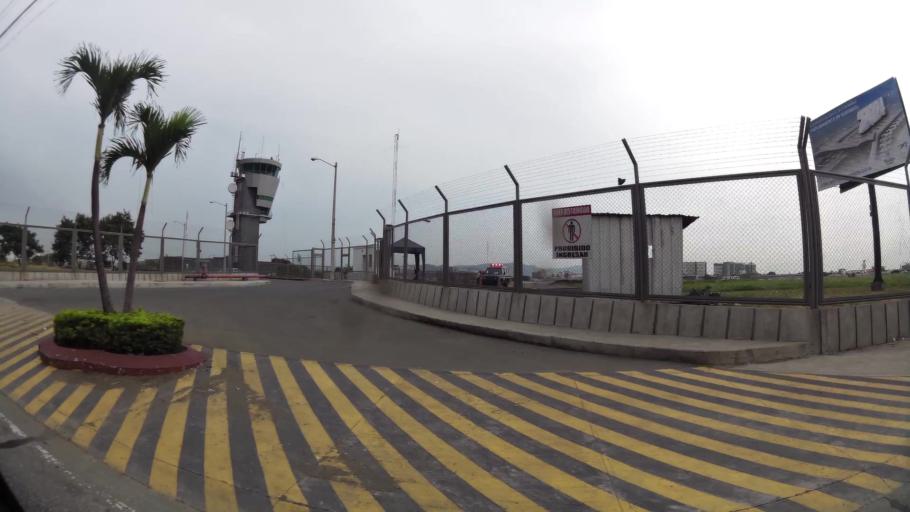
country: EC
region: Guayas
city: Eloy Alfaro
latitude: -2.1596
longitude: -79.8805
